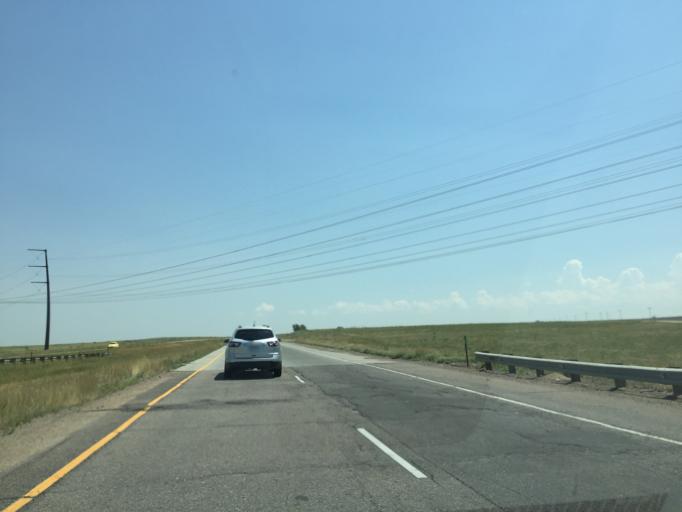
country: US
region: Colorado
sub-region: Arapahoe County
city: Byers
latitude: 39.6677
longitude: -104.0919
